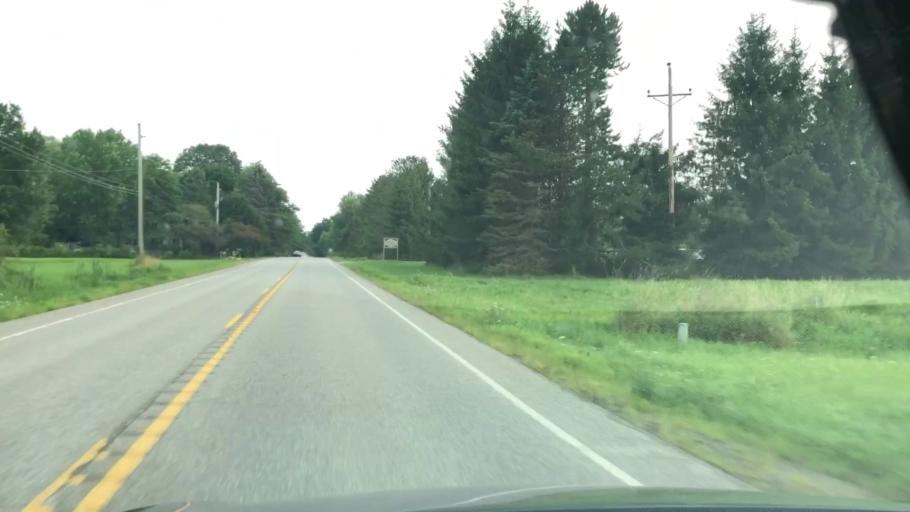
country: US
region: Pennsylvania
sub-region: Erie County
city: Union City
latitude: 41.9274
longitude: -79.8435
